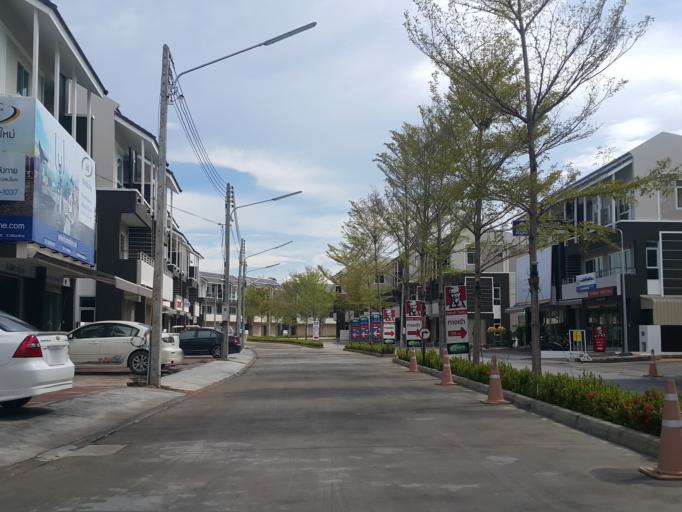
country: TH
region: Chiang Mai
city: Chiang Mai
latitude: 18.7568
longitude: 99.0004
